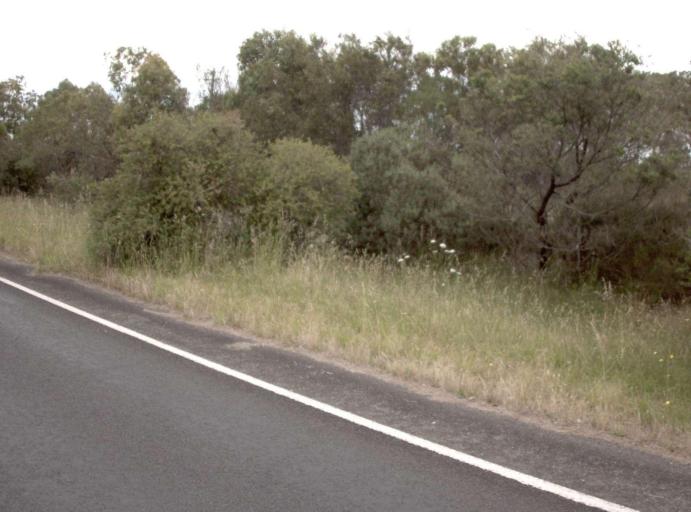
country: AU
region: Victoria
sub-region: Cardinia
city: Koo-Wee-Rup
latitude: -38.2927
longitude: 145.5454
